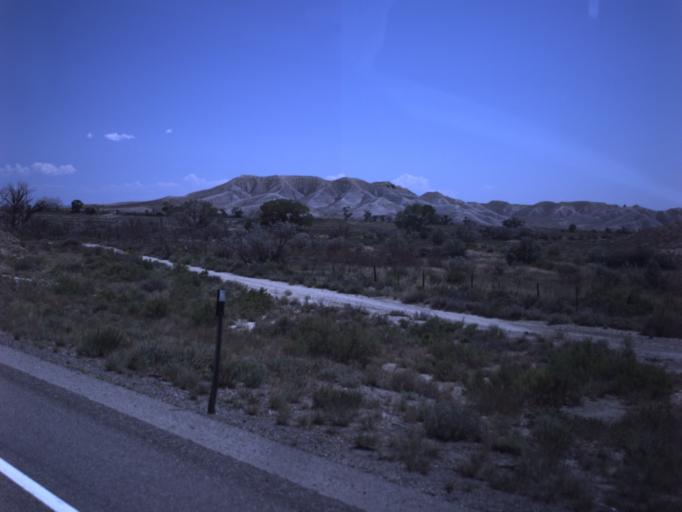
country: US
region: Utah
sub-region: Emery County
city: Ferron
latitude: 39.1202
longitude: -111.1163
